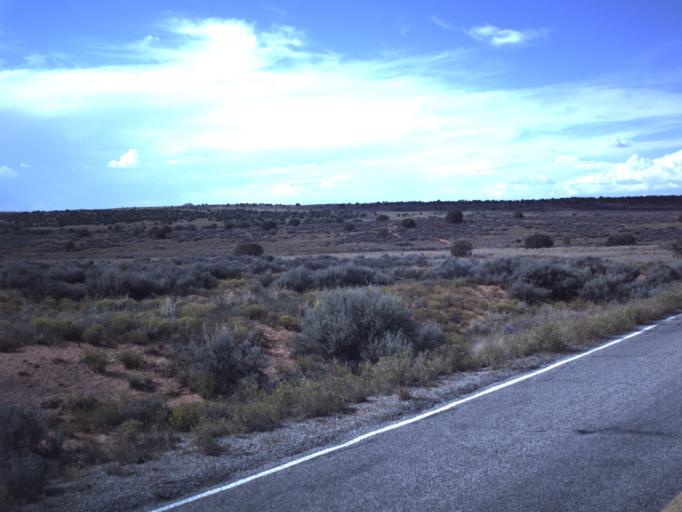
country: US
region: Utah
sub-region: Grand County
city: Moab
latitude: 38.5118
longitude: -109.7292
